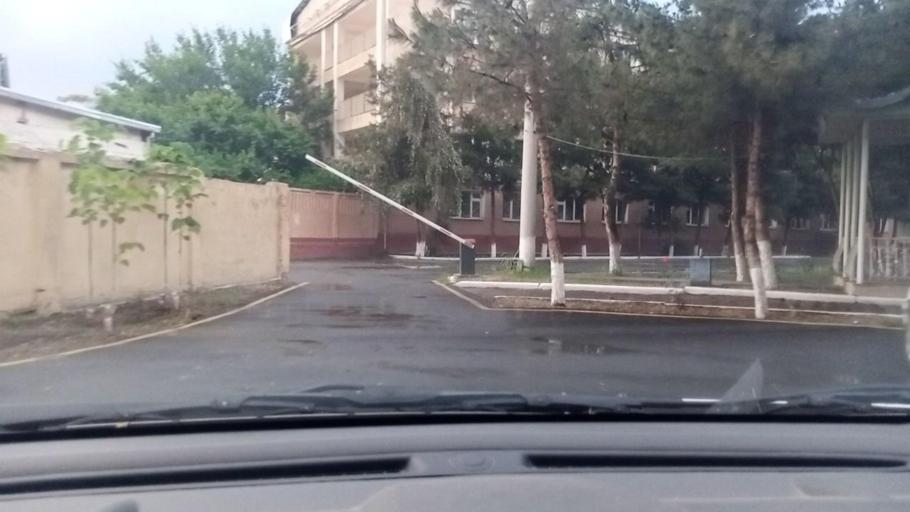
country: UZ
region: Toshkent Shahri
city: Tashkent
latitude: 41.2802
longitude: 69.2837
